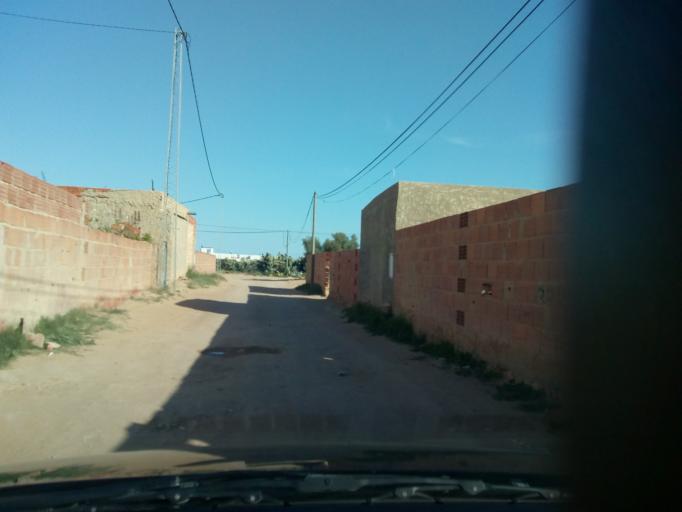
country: TN
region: Safaqis
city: Sfax
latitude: 34.7273
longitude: 10.6258
